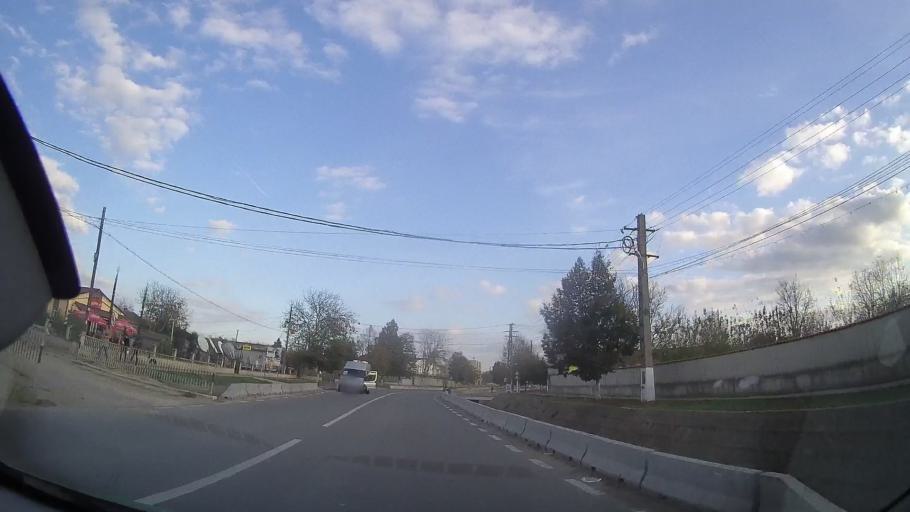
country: RO
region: Constanta
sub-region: Comuna Independenta
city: Independenta
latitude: 43.9515
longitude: 28.0826
